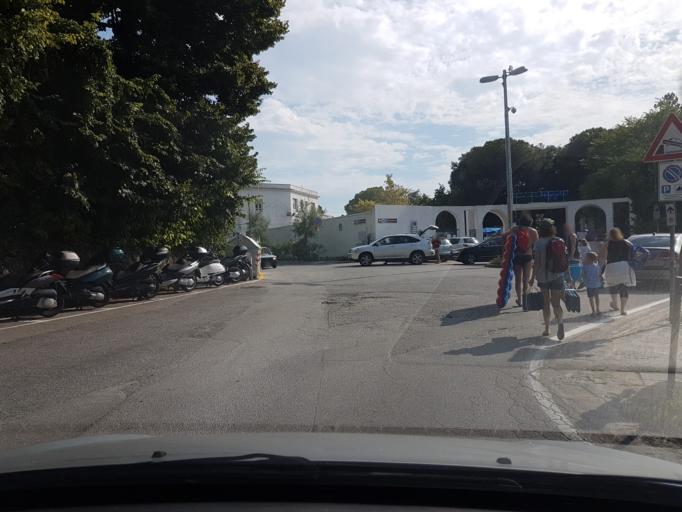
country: IT
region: Friuli Venezia Giulia
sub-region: Provincia di Trieste
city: Sistiana-Visogliano
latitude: 45.7686
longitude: 13.6327
